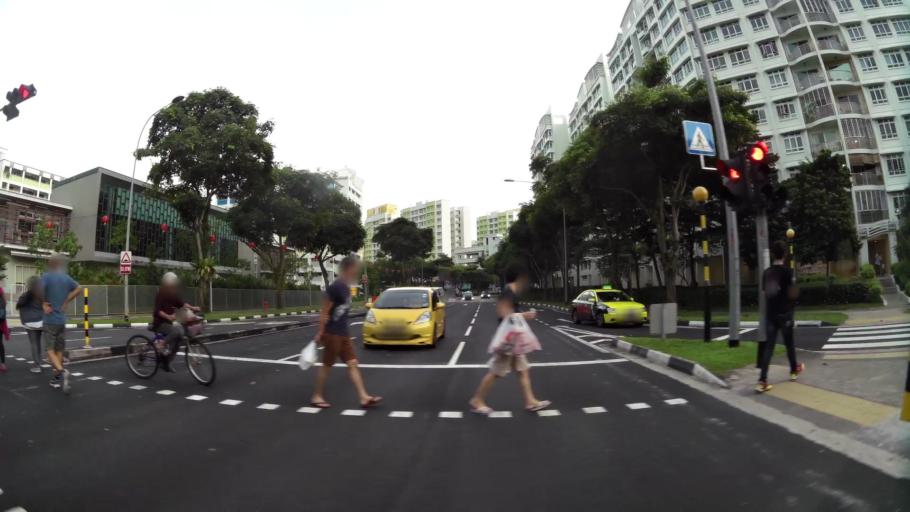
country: MY
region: Johor
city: Kampung Pasir Gudang Baru
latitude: 1.4242
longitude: 103.8450
